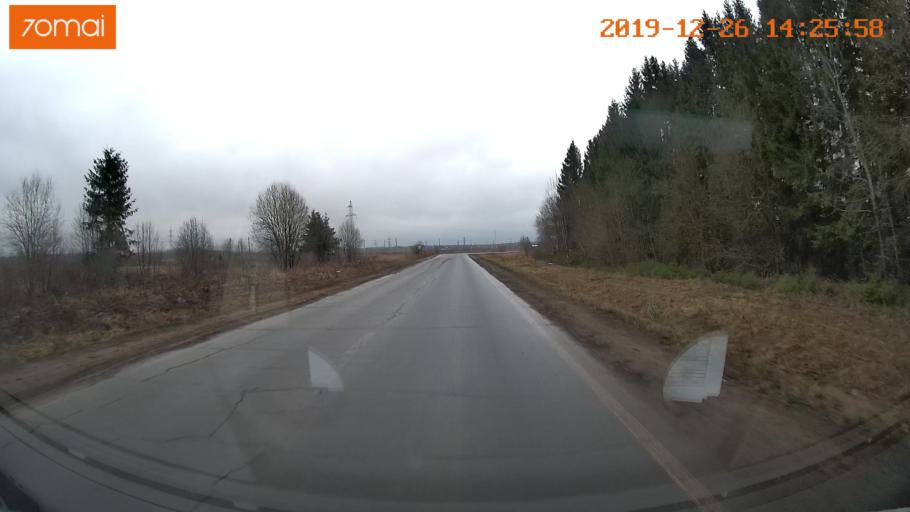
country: RU
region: Jaroslavl
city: Poshekhon'ye
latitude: 58.4898
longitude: 39.0910
